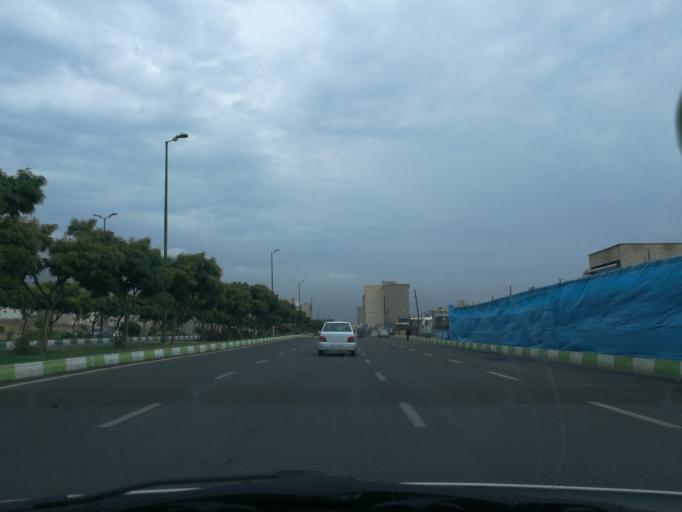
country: IR
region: Alborz
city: Karaj
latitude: 35.8539
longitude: 50.9589
